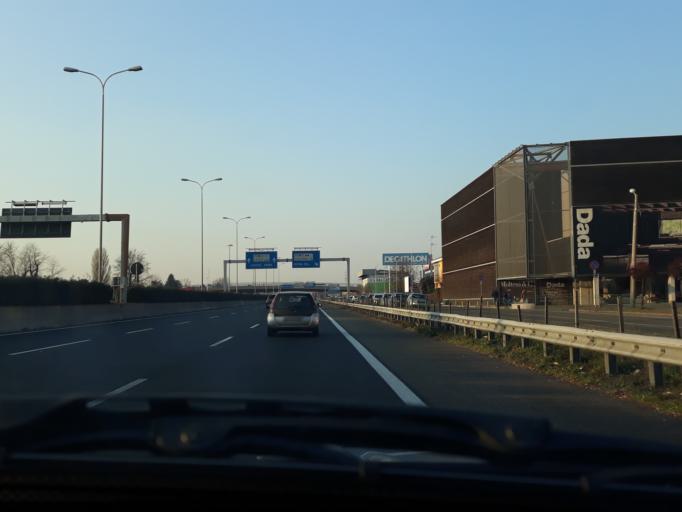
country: IT
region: Lombardy
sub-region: Provincia di Monza e Brianza
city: Lissone
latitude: 45.6035
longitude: 9.2298
